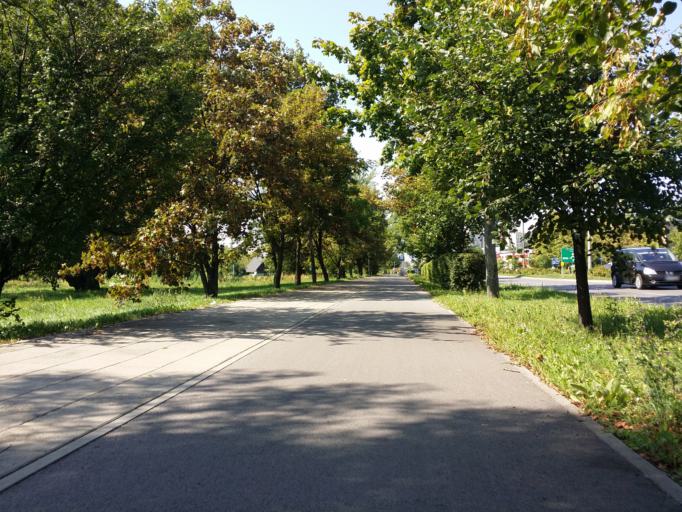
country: PL
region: Masovian Voivodeship
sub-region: Radom
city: Radom
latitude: 51.3827
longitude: 21.1640
